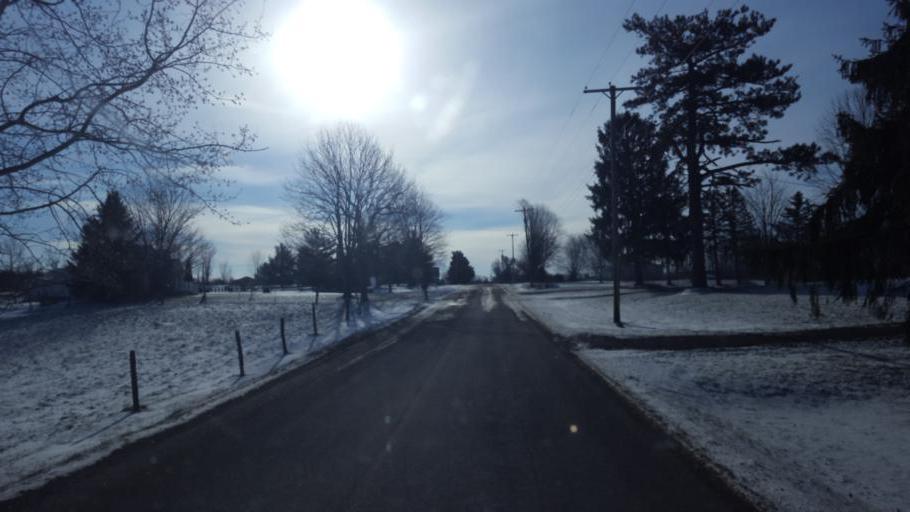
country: US
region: Ohio
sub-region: Morrow County
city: Mount Gilead
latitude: 40.5780
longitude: -82.7272
